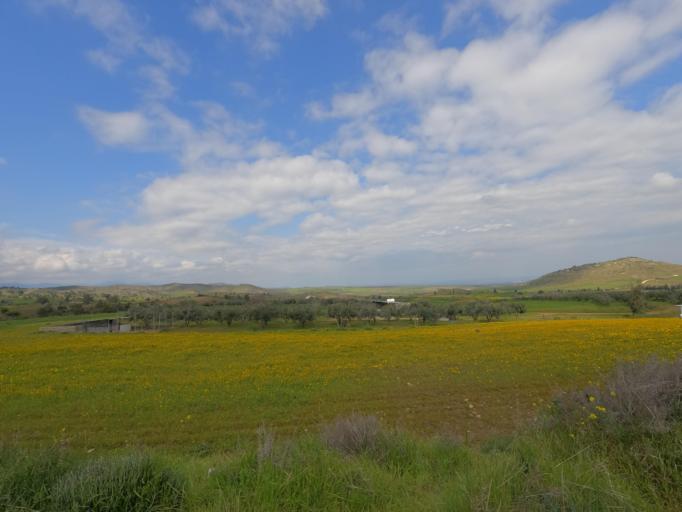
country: CY
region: Lefkosia
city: Astromeritis
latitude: 35.0777
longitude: 32.9609
